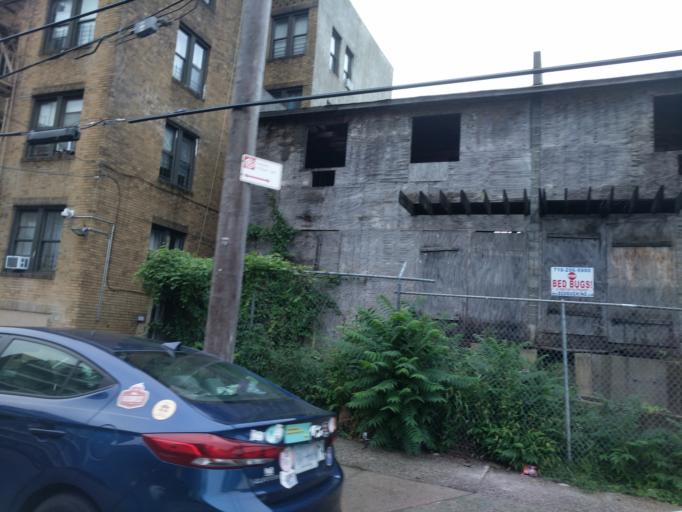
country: US
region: New York
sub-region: Nassau County
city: Inwood
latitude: 40.6085
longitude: -73.7479
